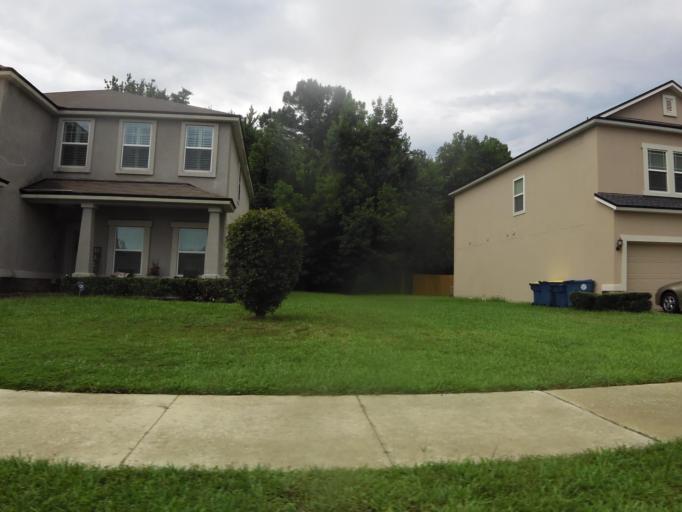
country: US
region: Florida
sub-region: Nassau County
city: Nassau Village-Ratliff
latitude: 30.4468
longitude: -81.7546
